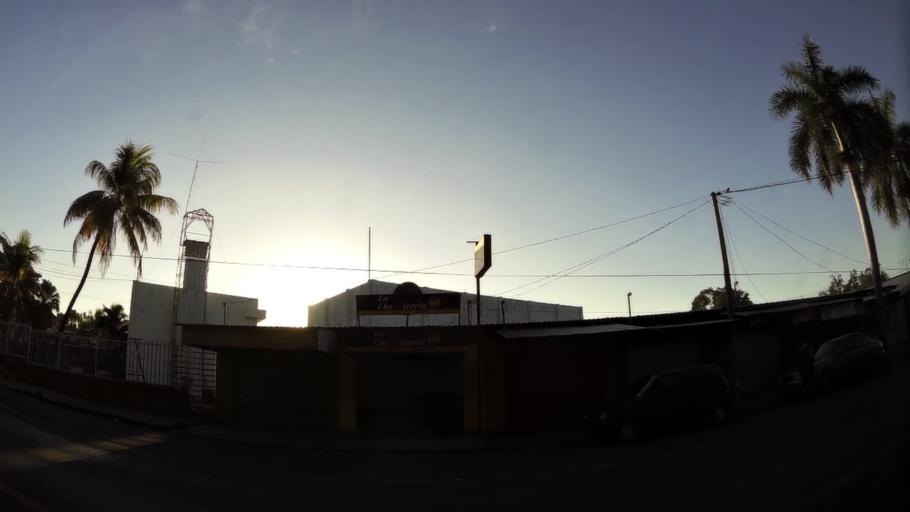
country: SV
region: Sonsonate
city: Sonsonate
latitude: 13.7157
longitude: -89.7243
